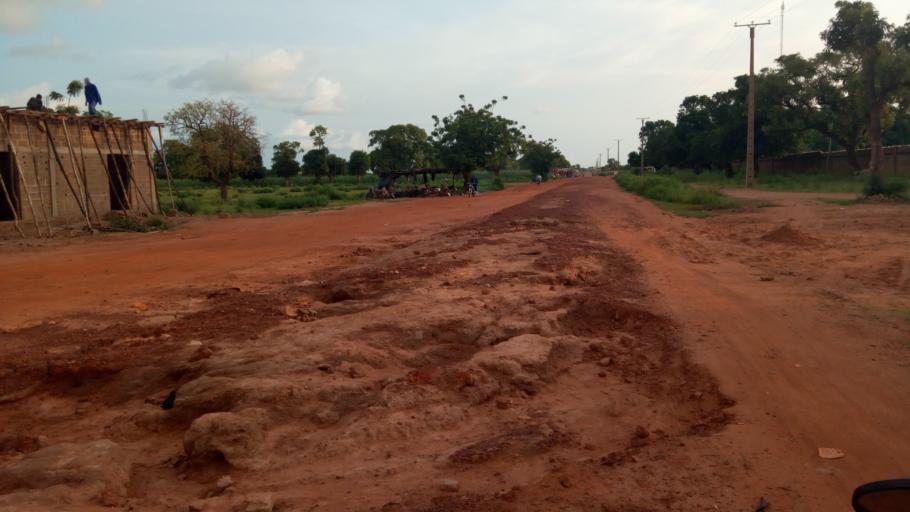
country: ML
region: Sikasso
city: Koutiala
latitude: 12.3739
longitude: -5.4749
